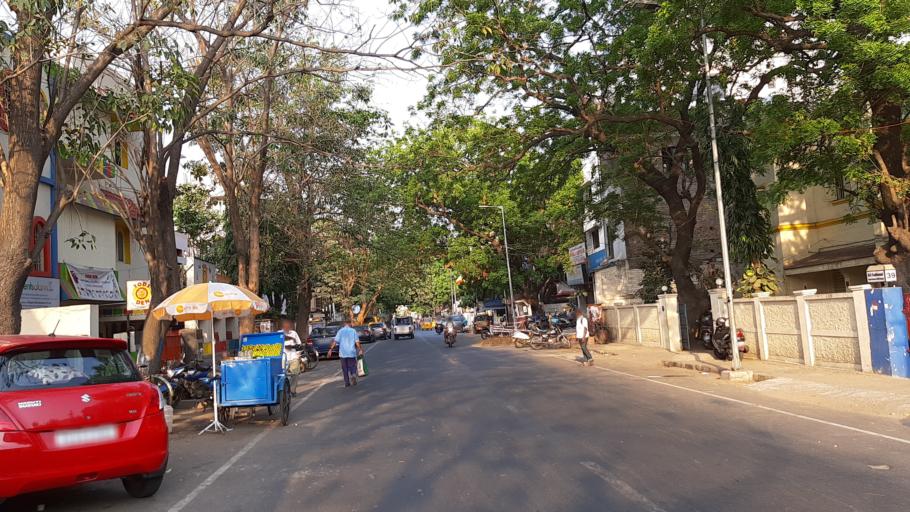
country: IN
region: Tamil Nadu
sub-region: Chennai
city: Gandhi Nagar
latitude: 13.0345
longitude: 80.2342
